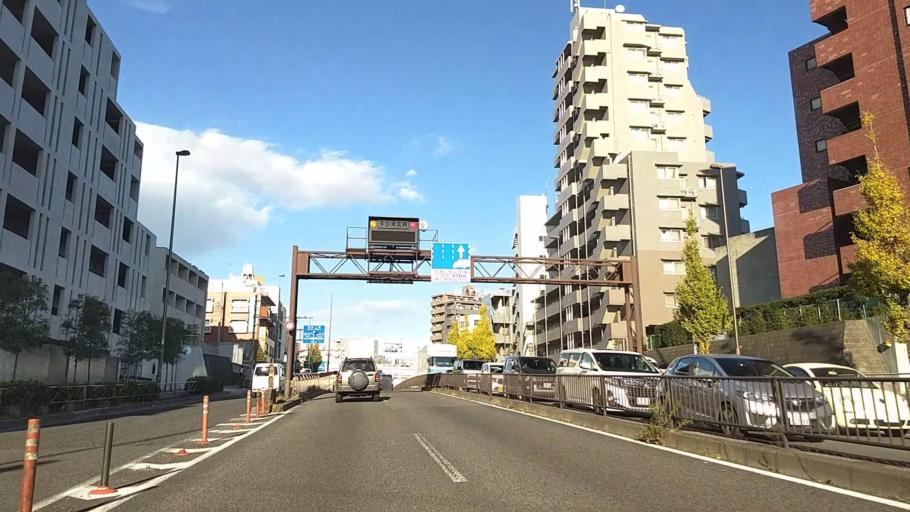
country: JP
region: Tokyo
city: Chofugaoka
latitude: 35.6194
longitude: 139.6295
